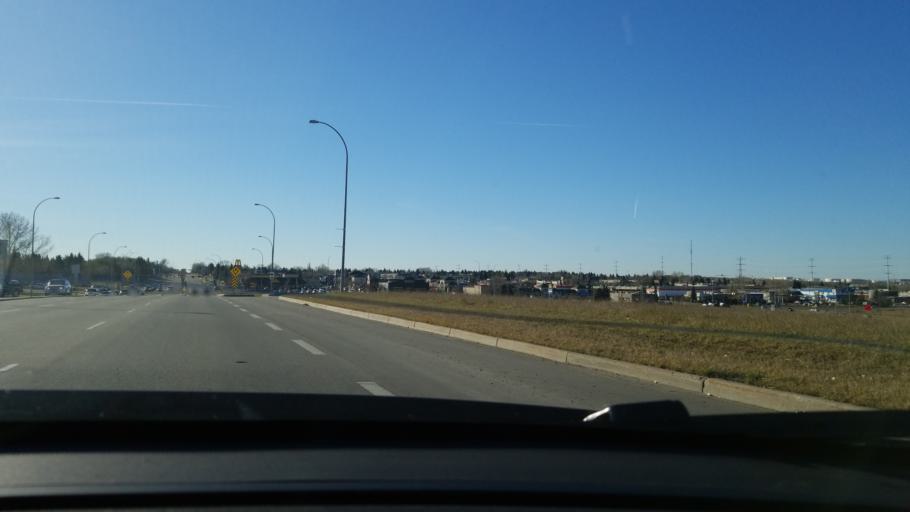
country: CA
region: Alberta
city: Sherwood Park
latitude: 53.5437
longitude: -113.3201
